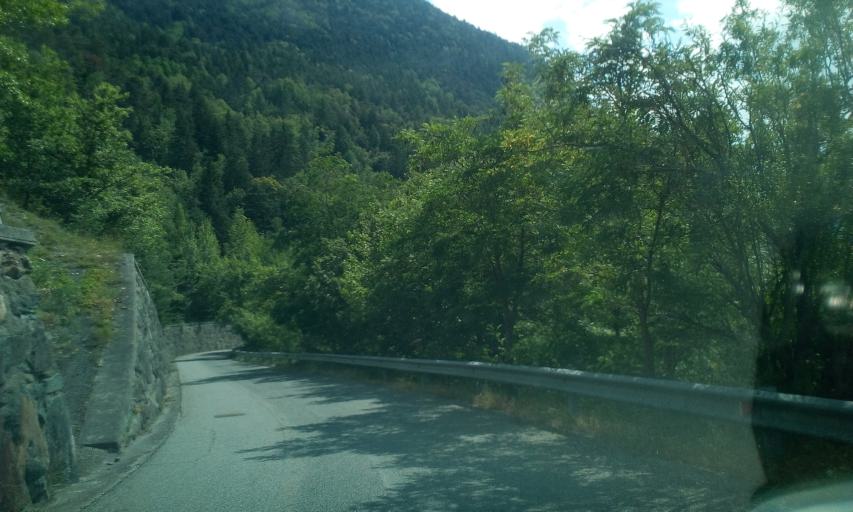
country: IT
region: Aosta Valley
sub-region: Valle d'Aosta
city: Jovencan
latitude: 45.7101
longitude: 7.2759
